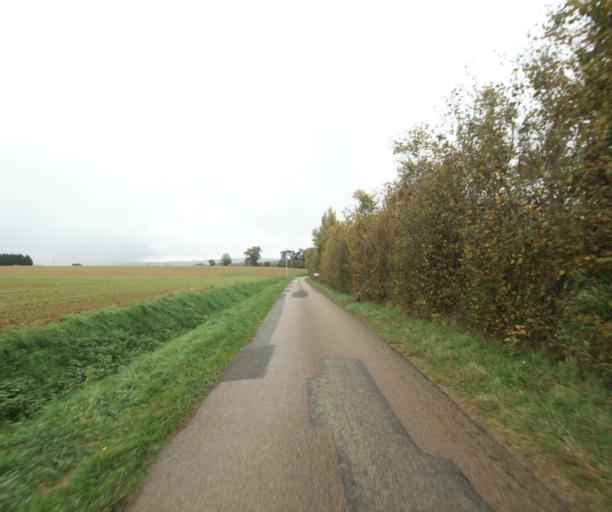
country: FR
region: Rhone-Alpes
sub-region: Departement de l'Ain
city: Pont-de-Vaux
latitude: 46.4793
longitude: 4.8719
